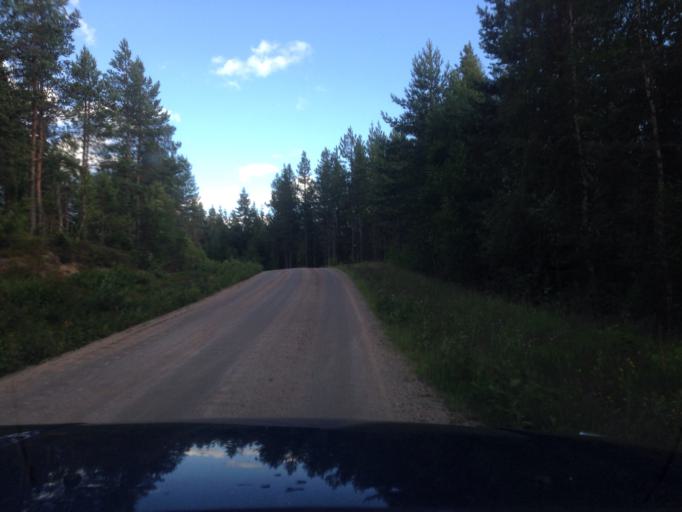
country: SE
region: Dalarna
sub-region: Vansbro Kommun
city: Jarna
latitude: 60.3285
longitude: 14.5610
